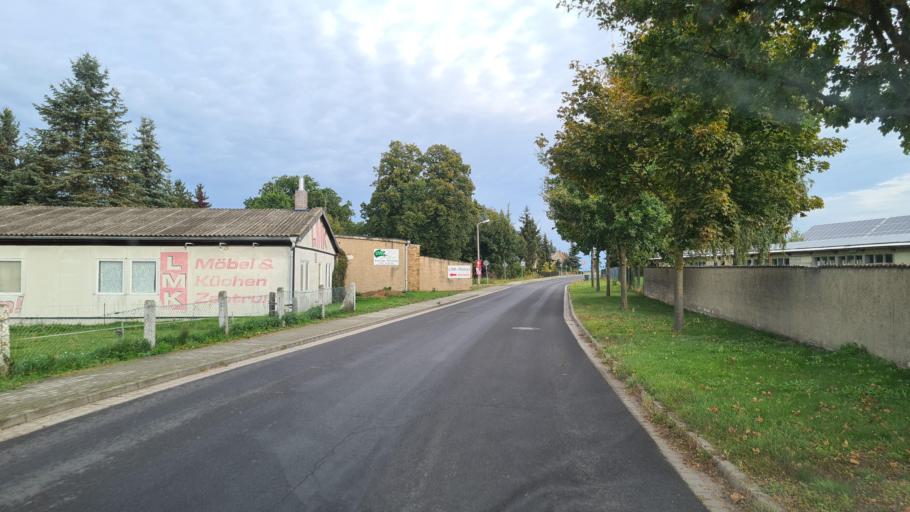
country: DE
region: Brandenburg
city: Luckau
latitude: 51.8709
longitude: 13.7237
